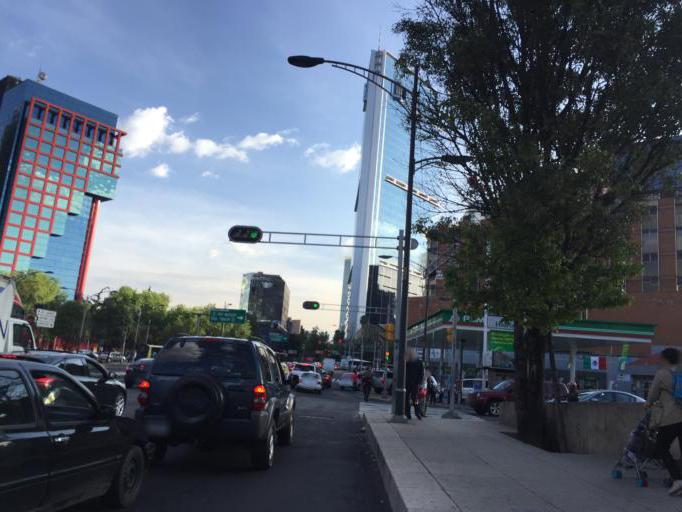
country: MX
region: Mexico City
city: Cuauhtemoc
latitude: 19.4322
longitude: -99.1592
